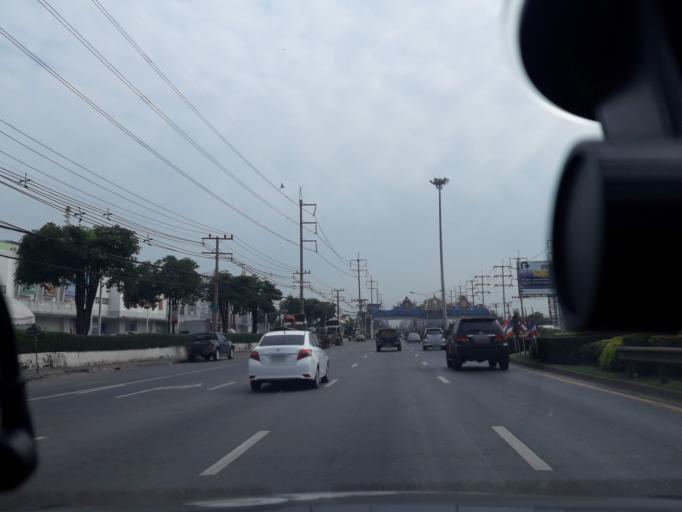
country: TH
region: Pathum Thani
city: Lam Luk Ka
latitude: 13.9339
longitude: 100.7129
